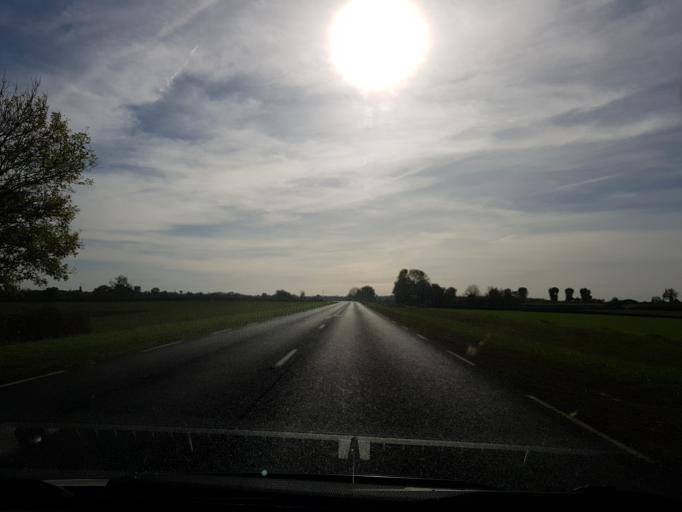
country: FR
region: Bourgogne
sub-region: Departement de l'Yonne
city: Avallon
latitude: 47.4924
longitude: 3.9901
